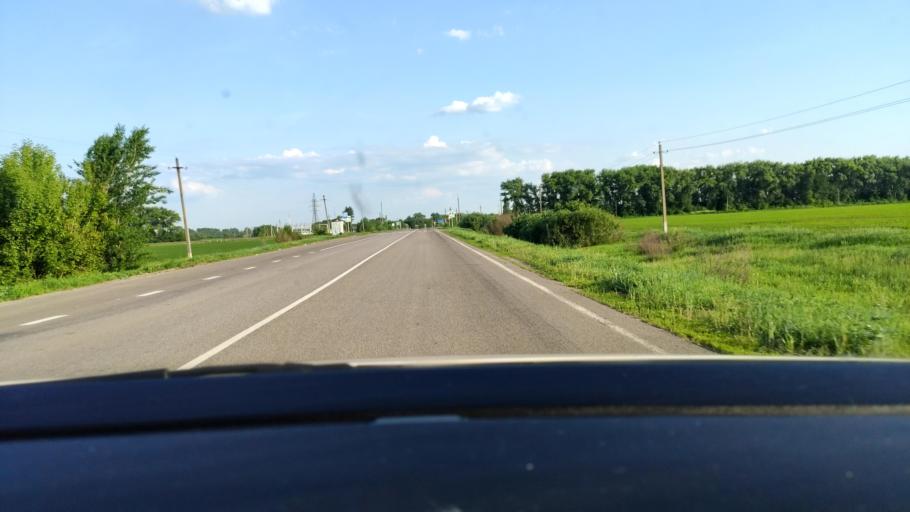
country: RU
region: Voronezj
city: Kashirskoye
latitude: 51.4706
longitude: 39.8622
